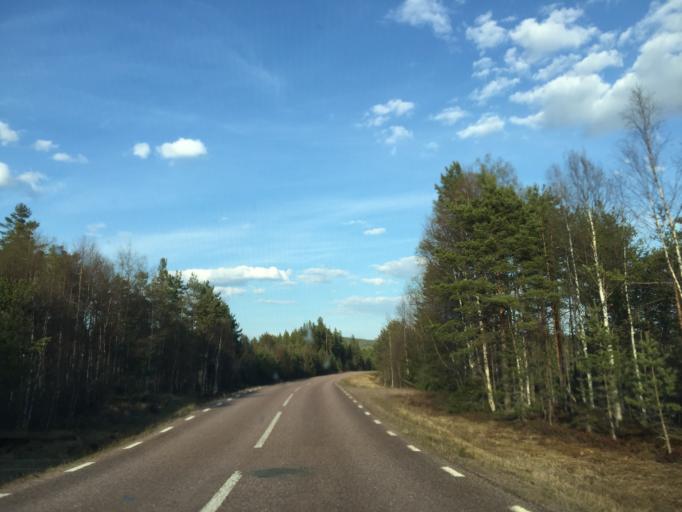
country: SE
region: Dalarna
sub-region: Vansbro Kommun
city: Jarna
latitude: 60.6407
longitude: 14.5813
